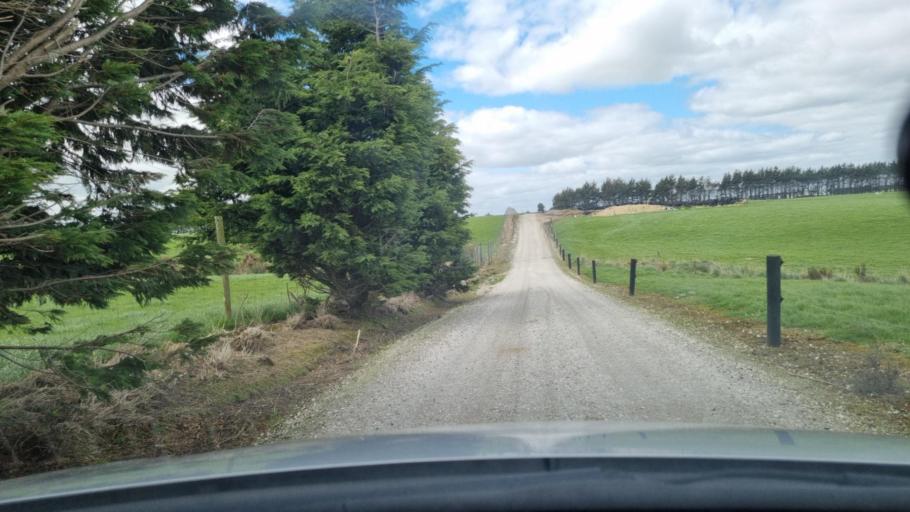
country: NZ
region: Southland
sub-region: Invercargill City
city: Invercargill
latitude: -46.4558
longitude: 168.4216
